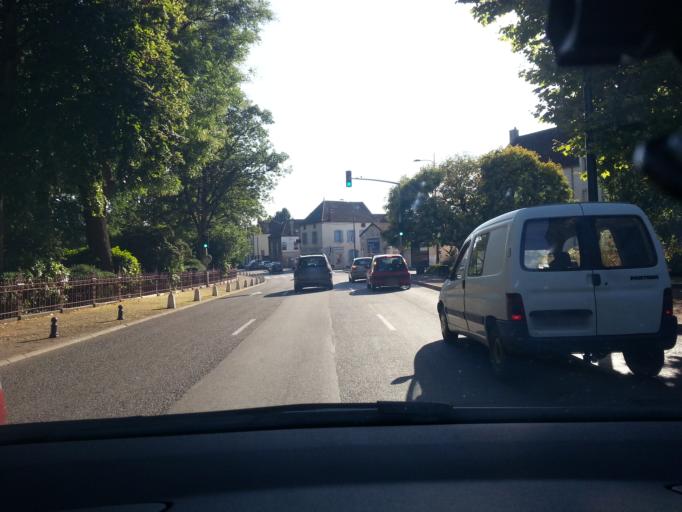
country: FR
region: Bourgogne
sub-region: Departement de la Cote-d'Or
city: Beaune
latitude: 47.0263
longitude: 4.8355
